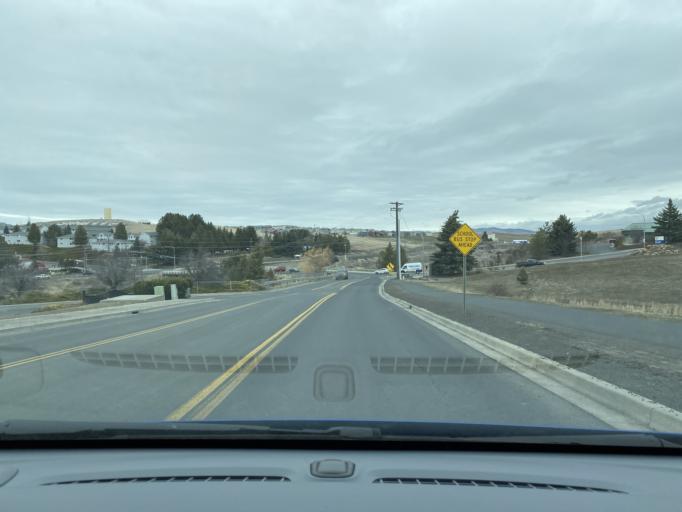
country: US
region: Washington
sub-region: Whitman County
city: Pullman
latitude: 46.7486
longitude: -117.1696
